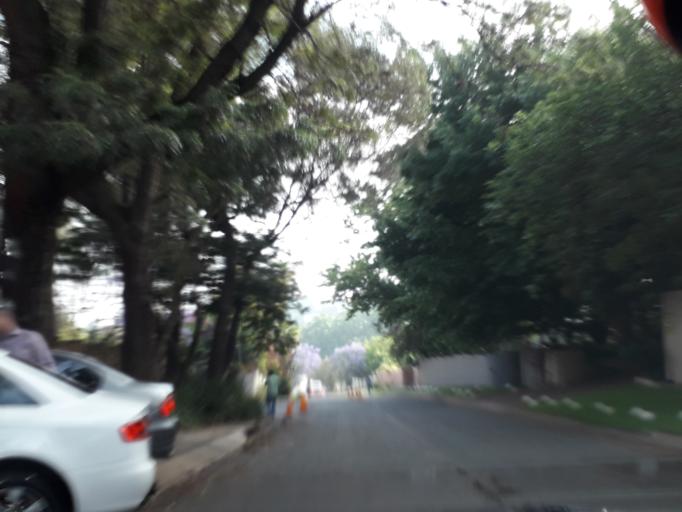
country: ZA
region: Gauteng
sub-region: City of Johannesburg Metropolitan Municipality
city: Johannesburg
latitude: -26.0954
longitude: 28.0436
